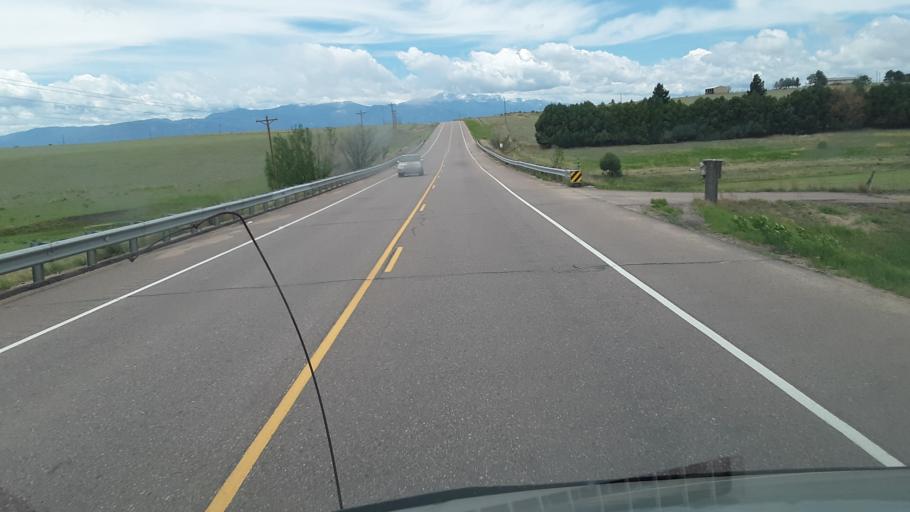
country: US
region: Colorado
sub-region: El Paso County
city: Cimarron Hills
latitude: 38.8387
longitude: -104.5640
